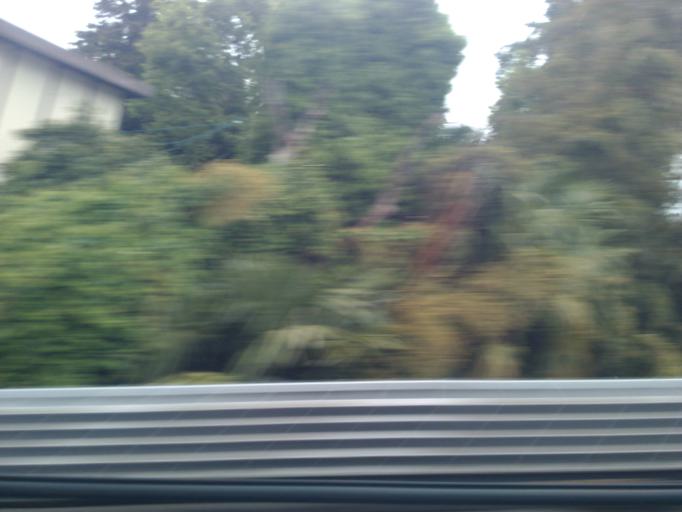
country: JP
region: Kanagawa
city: Yokohama
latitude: 35.4754
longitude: 139.5616
